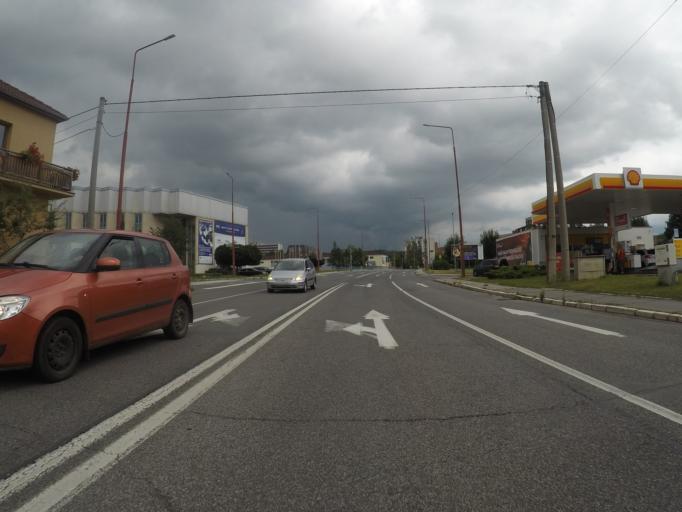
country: SK
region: Kosicky
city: Spisska Nova Ves
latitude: 48.9419
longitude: 20.5602
